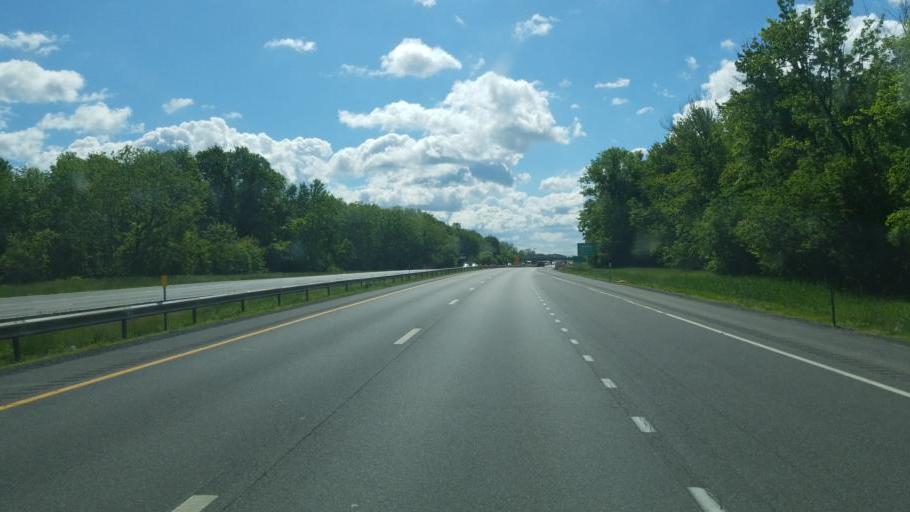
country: US
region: New York
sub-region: Onondaga County
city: Liverpool
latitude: 43.1153
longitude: -76.2123
